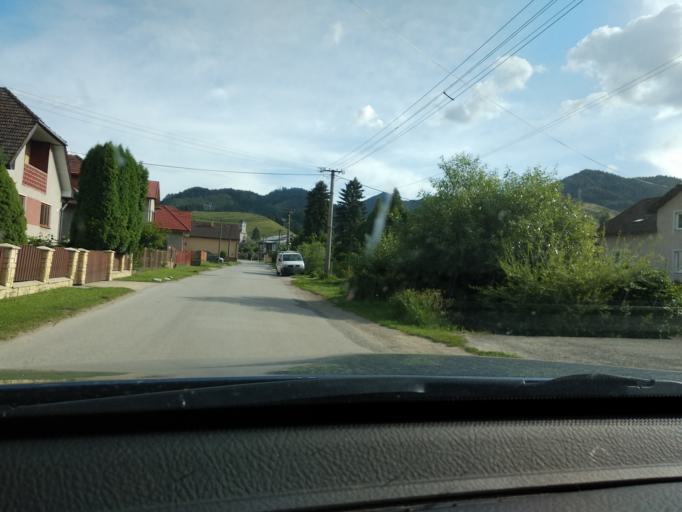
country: SK
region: Zilinsky
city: Ruzomberok
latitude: 49.0513
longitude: 19.3326
